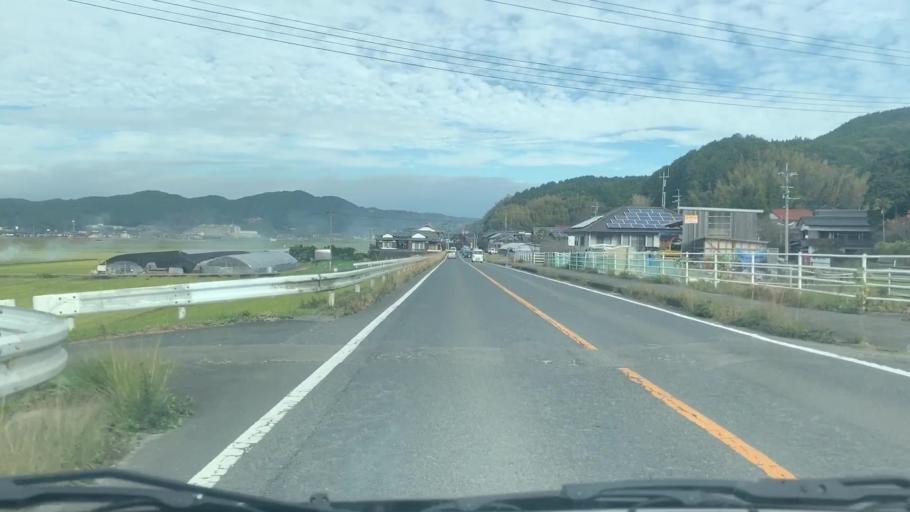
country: JP
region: Saga Prefecture
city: Karatsu
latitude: 33.3858
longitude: 129.9882
